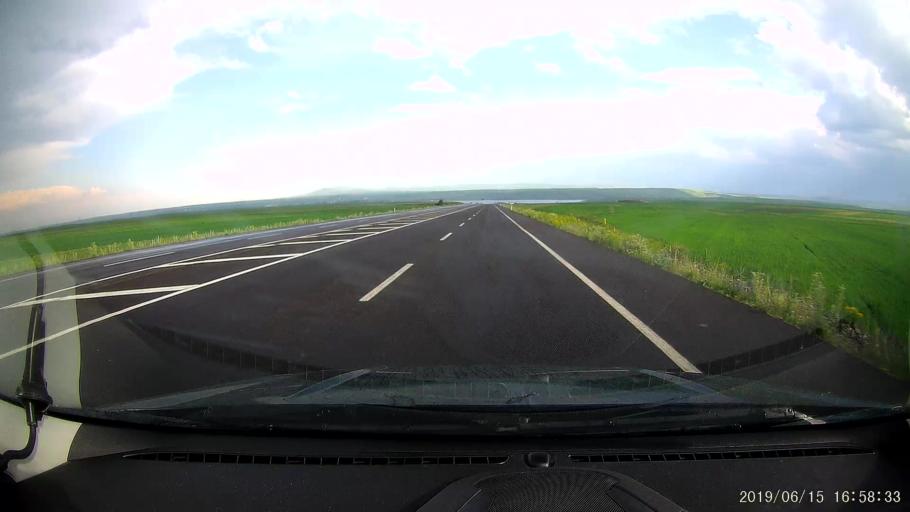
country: TR
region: Kars
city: Susuz
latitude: 40.7639
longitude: 43.1441
